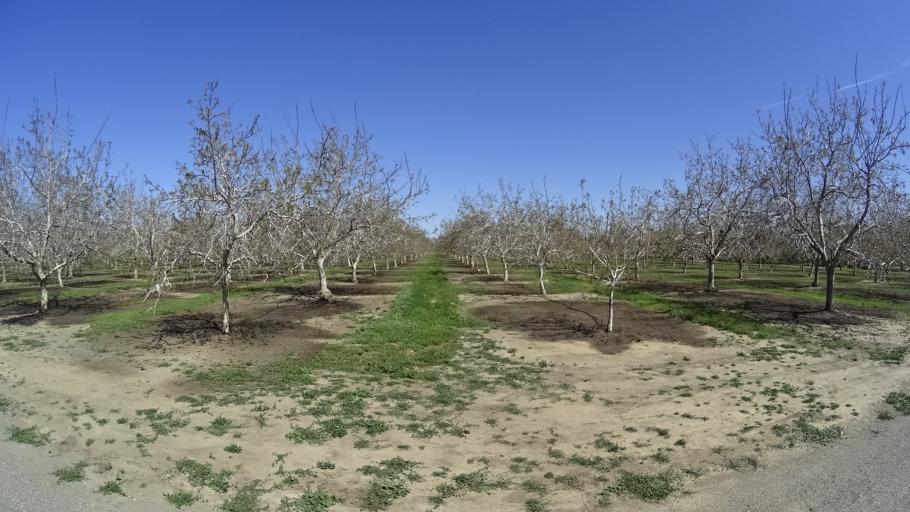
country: US
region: California
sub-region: Glenn County
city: Orland
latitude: 39.7431
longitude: -122.1212
